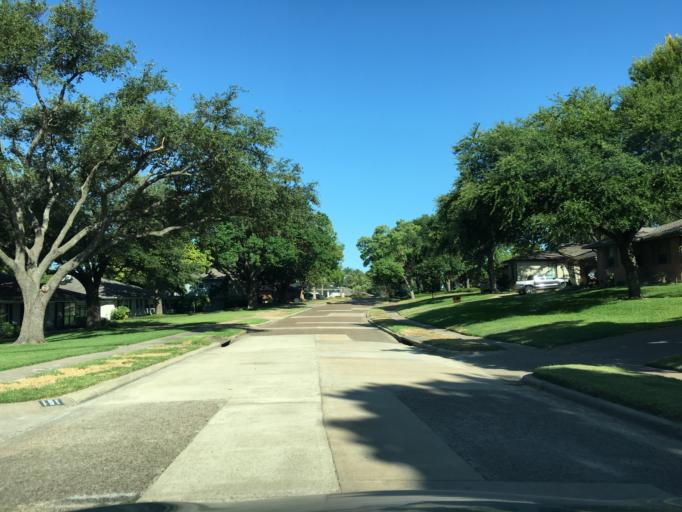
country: US
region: Texas
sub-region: Dallas County
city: Highland Park
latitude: 32.8603
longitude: -96.7131
